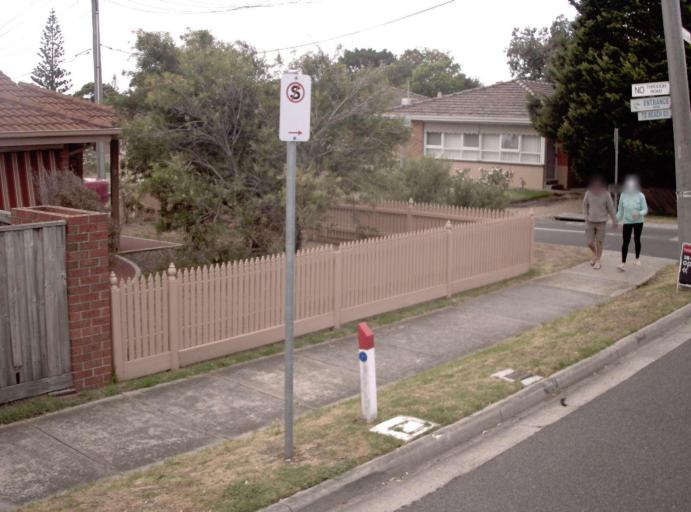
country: AU
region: Victoria
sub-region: Frankston
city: Seaford
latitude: -38.0982
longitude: 145.1258
